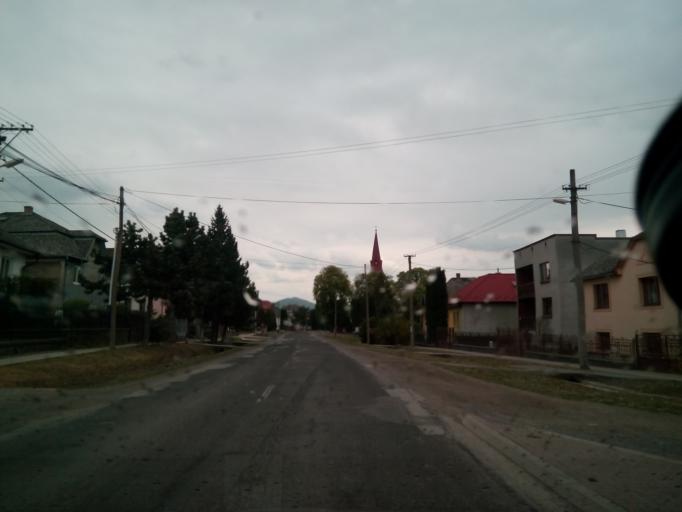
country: SK
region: Kosicky
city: Kosice
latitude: 48.7435
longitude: 21.4391
